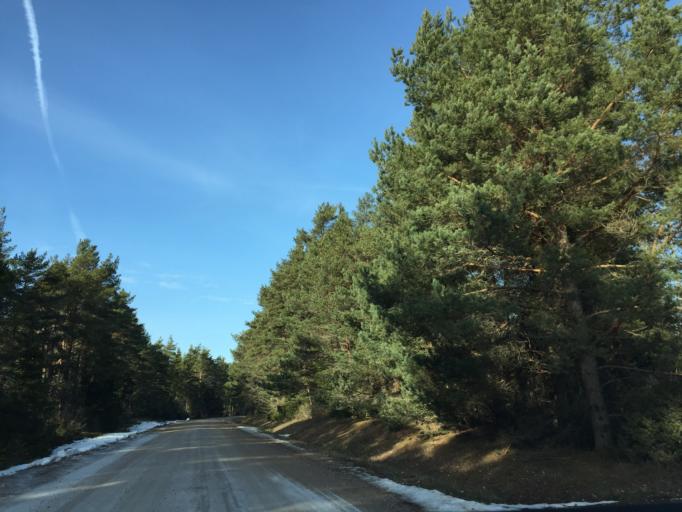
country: EE
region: Saare
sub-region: Kuressaare linn
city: Kuressaare
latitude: 58.3709
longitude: 22.0172
